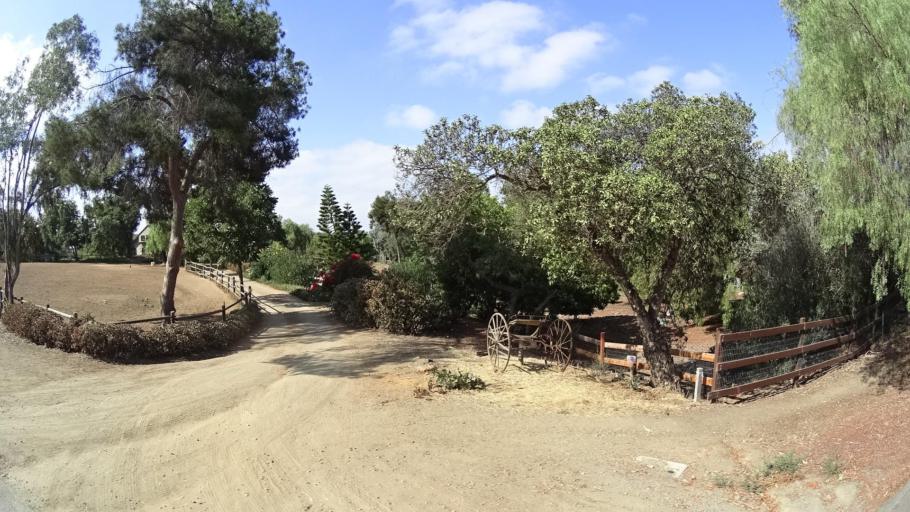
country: US
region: California
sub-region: San Diego County
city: Rancho Santa Fe
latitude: 33.0423
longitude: -117.1974
